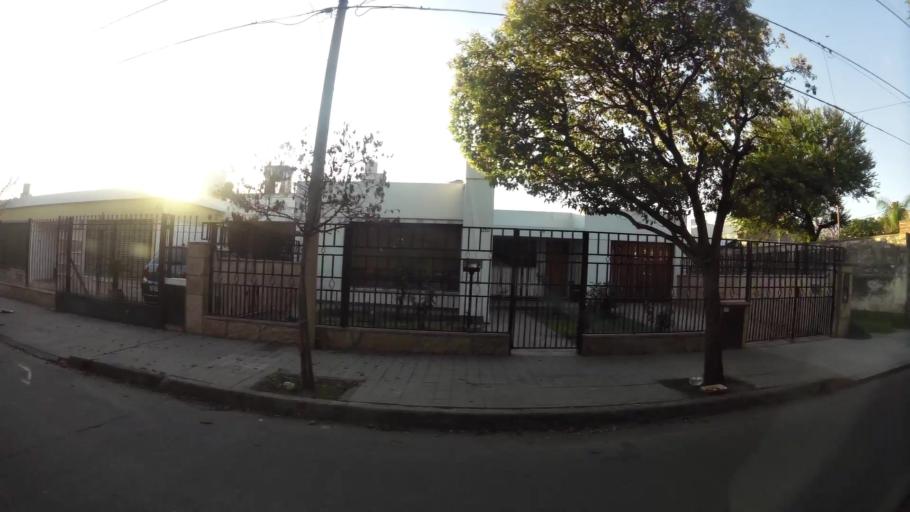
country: AR
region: Cordoba
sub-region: Departamento de Capital
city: Cordoba
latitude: -31.3848
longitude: -64.2157
